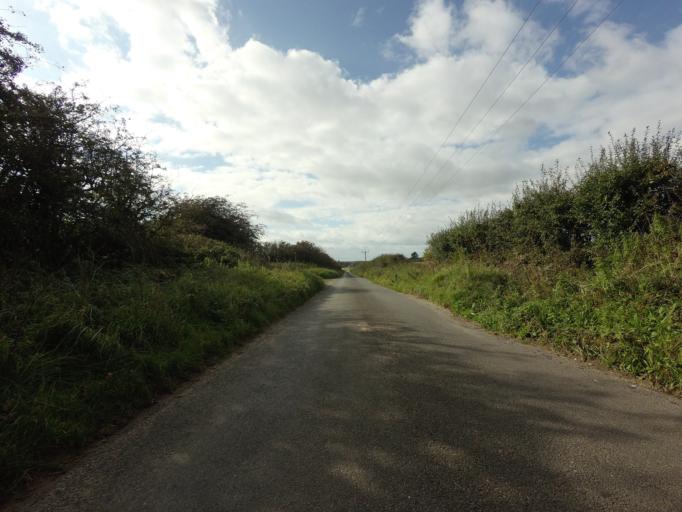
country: GB
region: England
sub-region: Norfolk
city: Hunstanton
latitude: 52.9353
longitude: 0.5768
